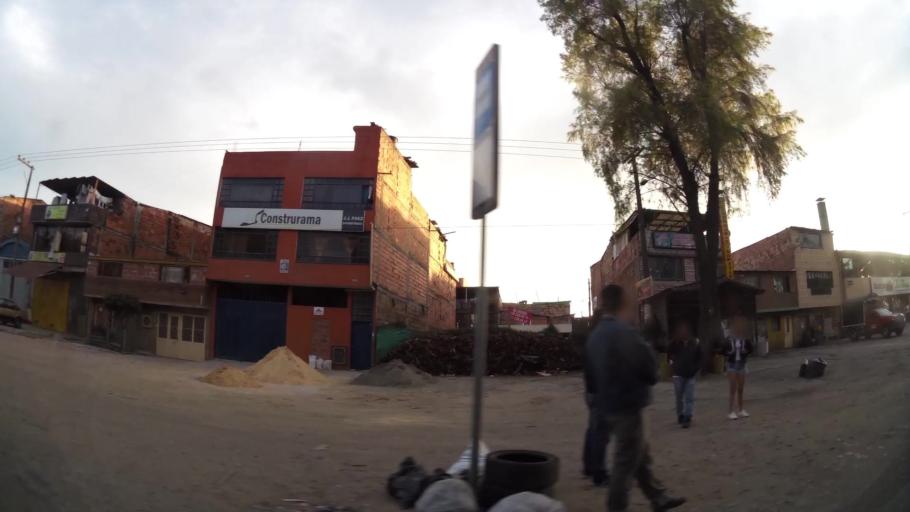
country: CO
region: Cundinamarca
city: Funza
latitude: 4.6944
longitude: -74.1506
